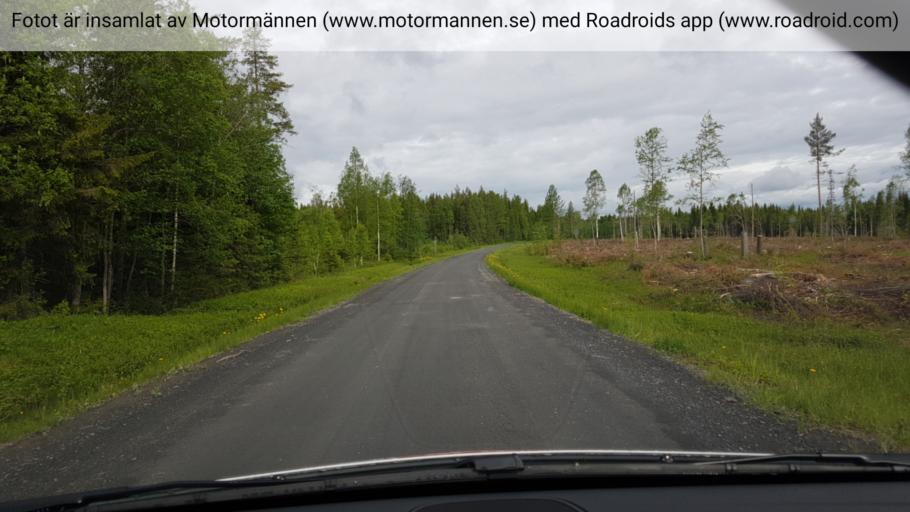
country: SE
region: Jaemtland
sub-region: OEstersunds Kommun
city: Lit
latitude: 63.2292
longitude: 15.0547
